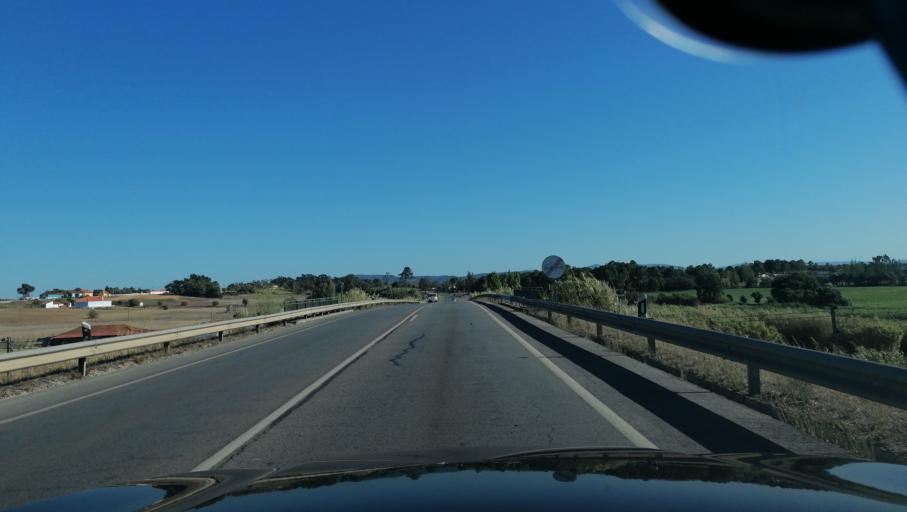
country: PT
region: Setubal
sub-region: Moita
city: Moita
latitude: 38.6407
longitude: -8.9717
